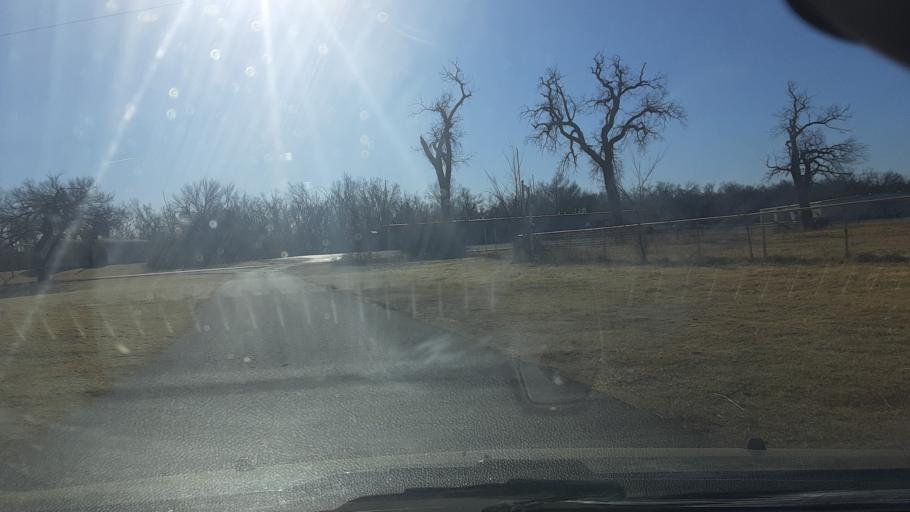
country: US
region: Oklahoma
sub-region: Logan County
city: Guthrie
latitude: 35.8670
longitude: -97.4274
